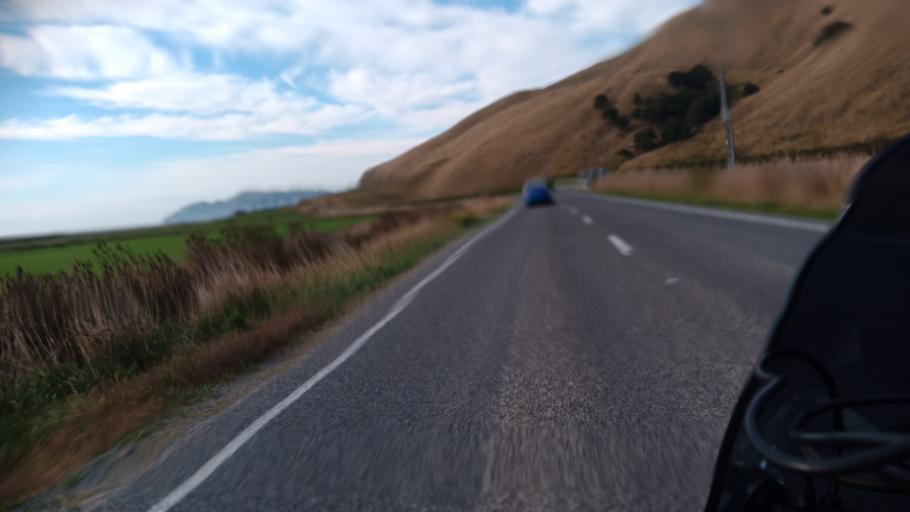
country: NZ
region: Gisborne
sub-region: Gisborne District
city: Gisborne
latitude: -38.7247
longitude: 177.9129
